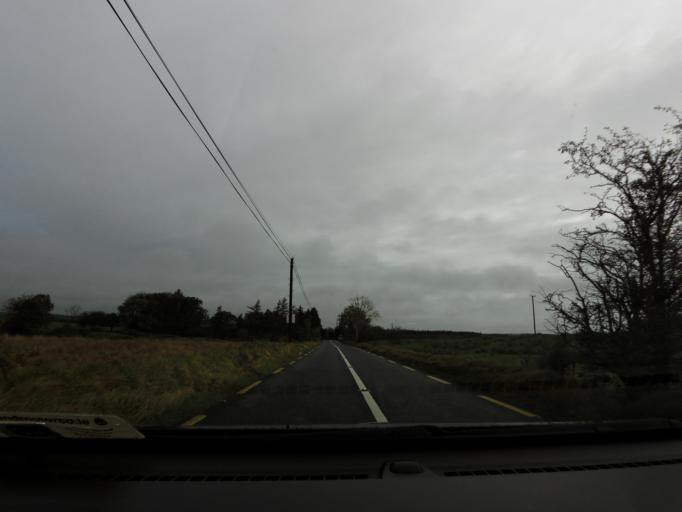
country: IE
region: Connaught
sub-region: Maigh Eo
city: Ballyhaunis
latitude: 53.6238
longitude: -8.7429
